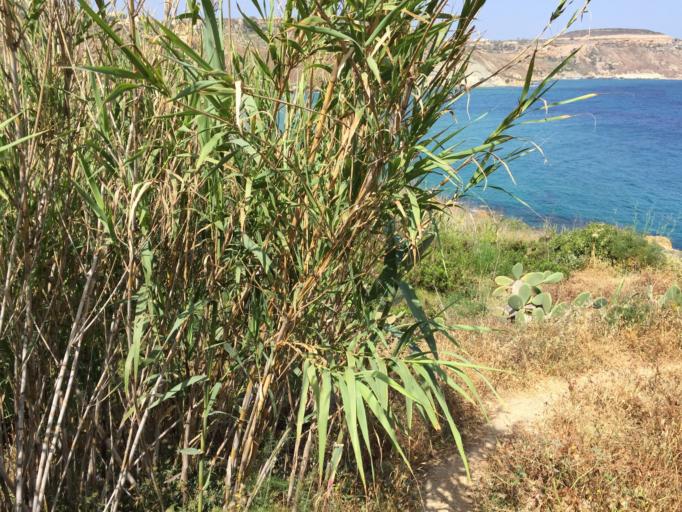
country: MT
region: In-Nadur
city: Nadur
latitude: 36.0632
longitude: 14.2887
